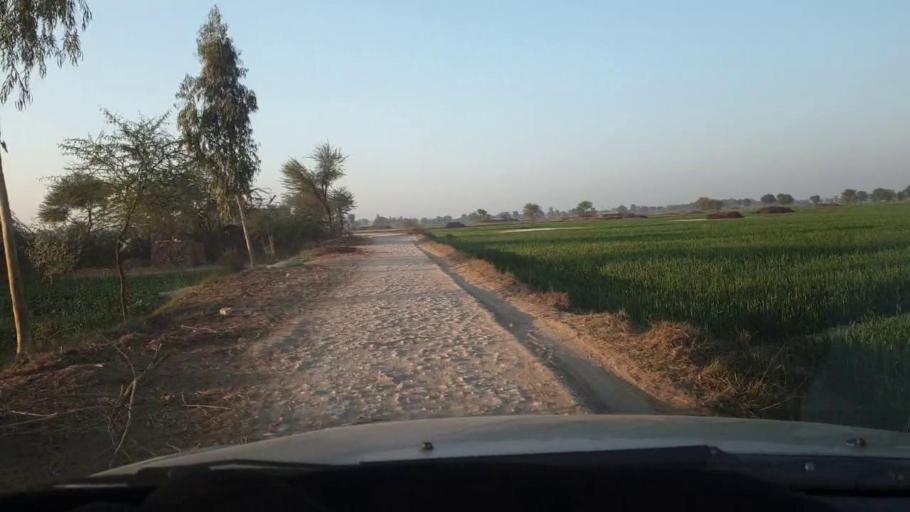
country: PK
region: Sindh
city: Mirpur Mathelo
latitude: 28.0027
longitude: 69.6033
